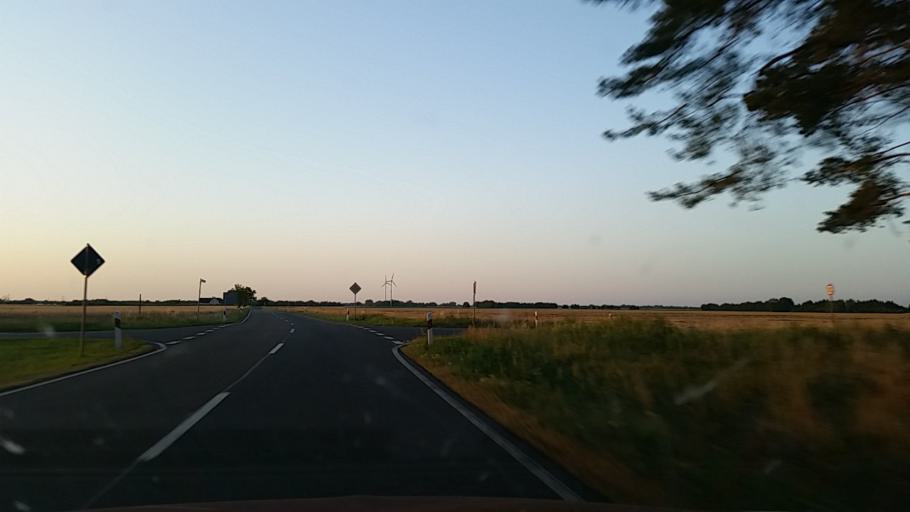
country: DE
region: Saxony-Anhalt
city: Prettin
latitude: 51.6937
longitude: 12.9267
